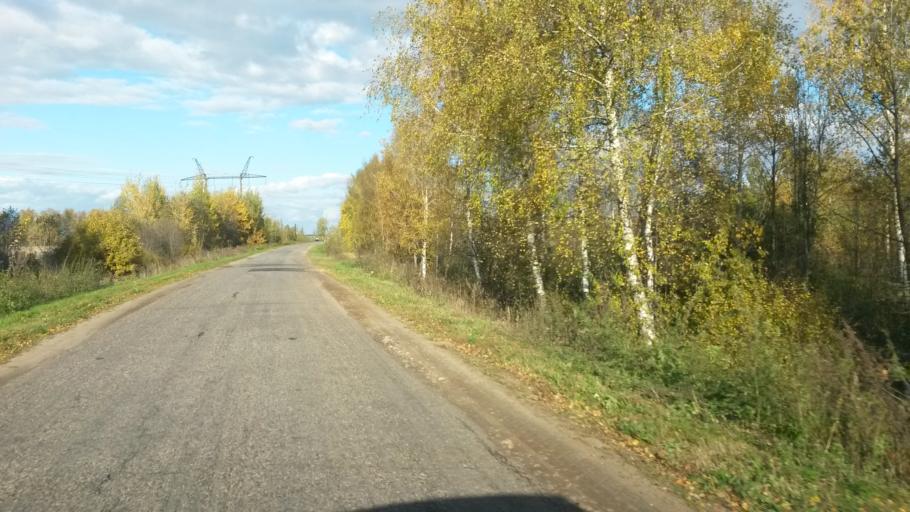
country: RU
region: Jaroslavl
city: Tunoshna
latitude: 57.5323
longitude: 40.0154
